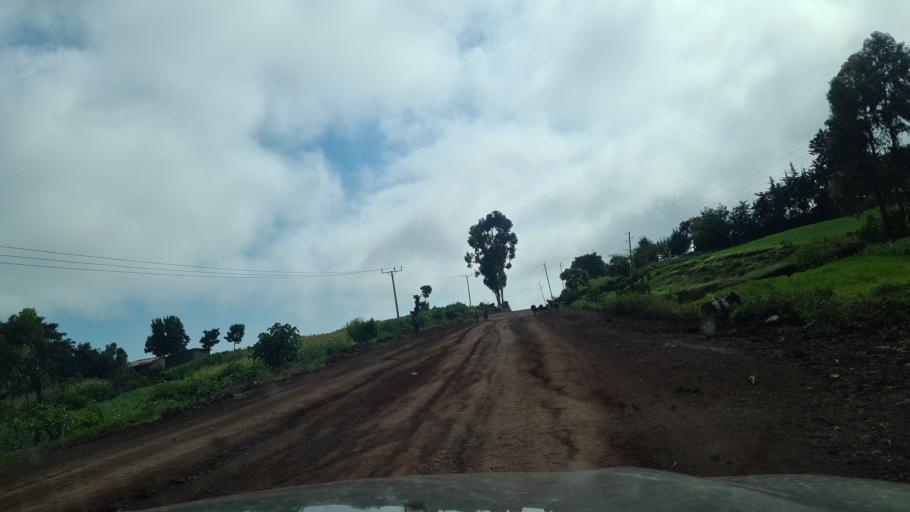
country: ET
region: Oromiya
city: Huruta
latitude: 8.1236
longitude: 39.3694
